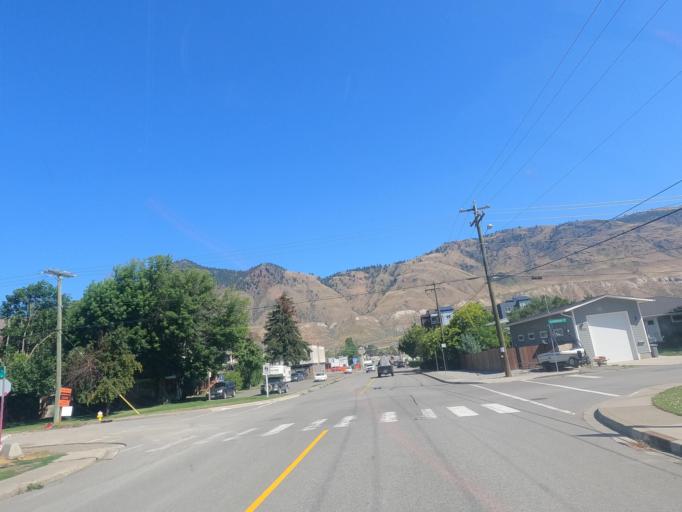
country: CA
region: British Columbia
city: Kamloops
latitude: 50.6770
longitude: -120.2723
